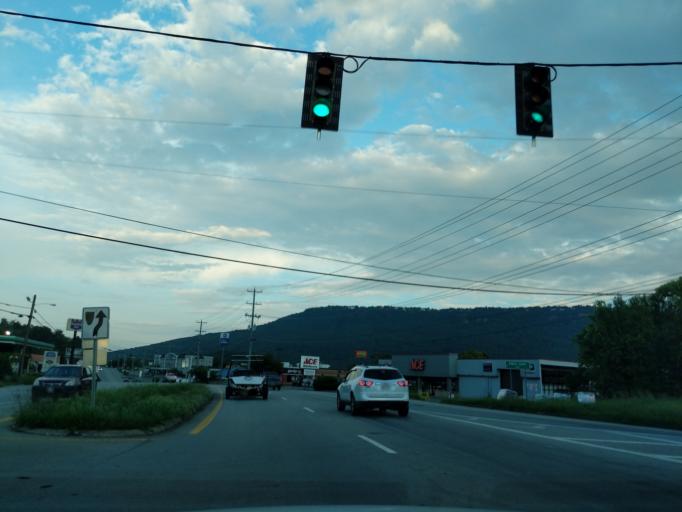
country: US
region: Tennessee
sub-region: Hamilton County
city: Lookout Mountain
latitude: 35.0181
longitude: -85.3809
